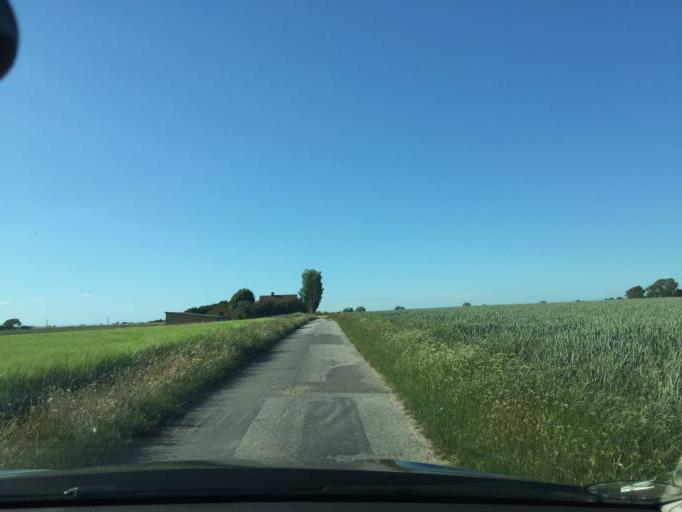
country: DK
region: Zealand
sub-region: Slagelse Kommune
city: Skaelskor
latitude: 55.2012
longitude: 11.1817
